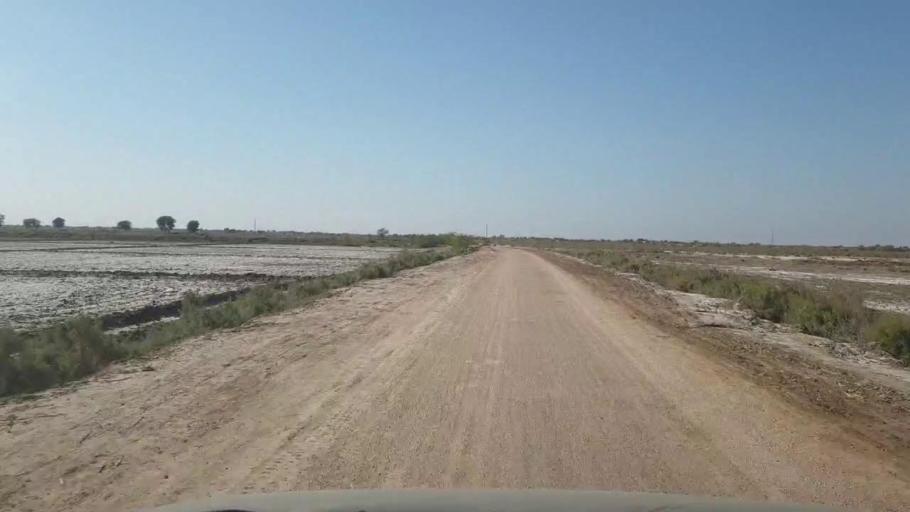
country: PK
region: Sindh
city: Samaro
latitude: 25.3695
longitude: 69.3110
